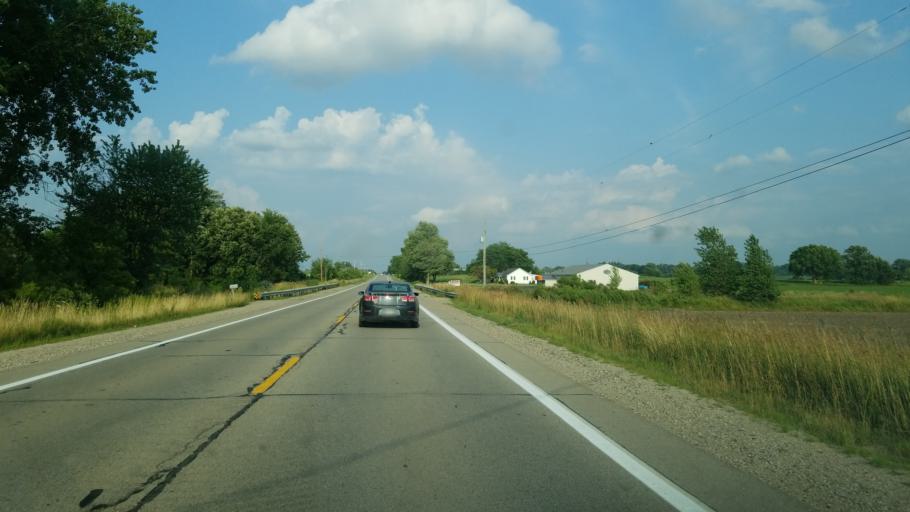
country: US
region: Michigan
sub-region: Gratiot County
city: Alma
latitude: 43.4082
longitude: -84.7039
